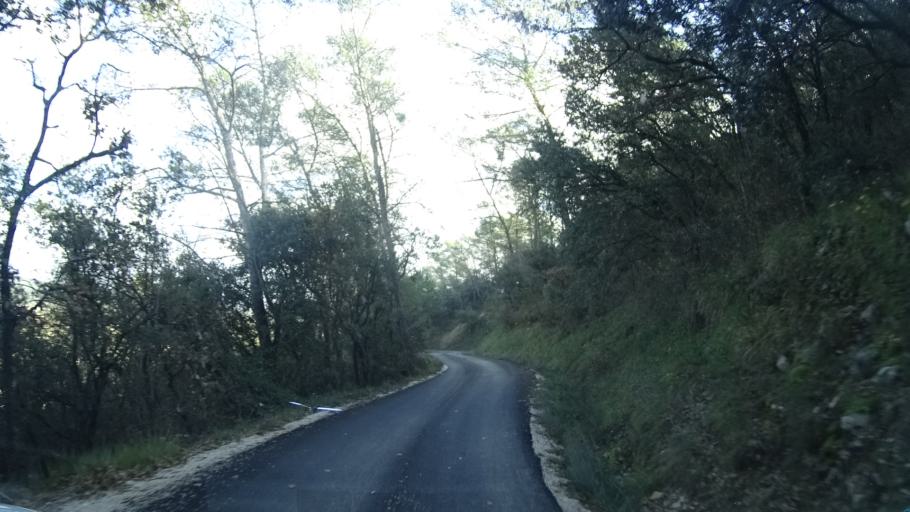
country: FR
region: Languedoc-Roussillon
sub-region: Departement de l'Herault
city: Claret
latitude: 43.8470
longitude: 3.8866
